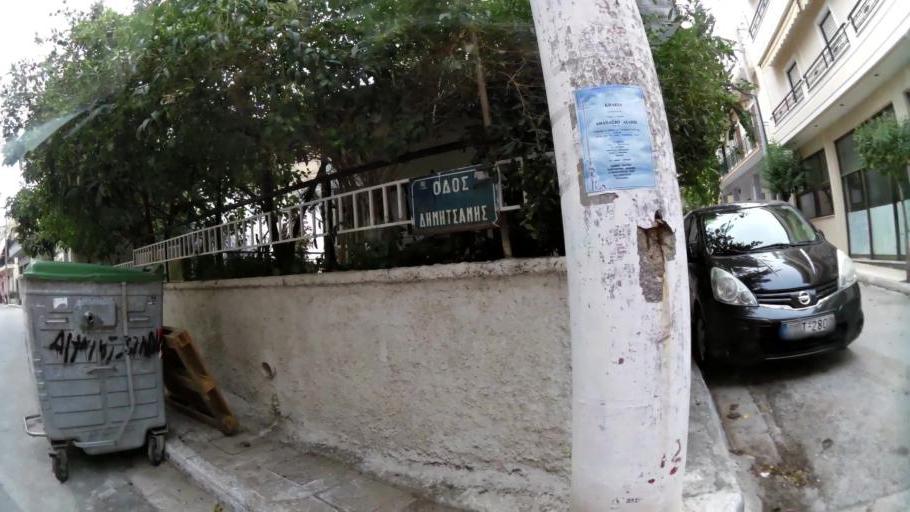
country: GR
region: Attica
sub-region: Nomarchia Athinas
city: Agioi Anargyroi
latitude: 38.0250
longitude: 23.7116
